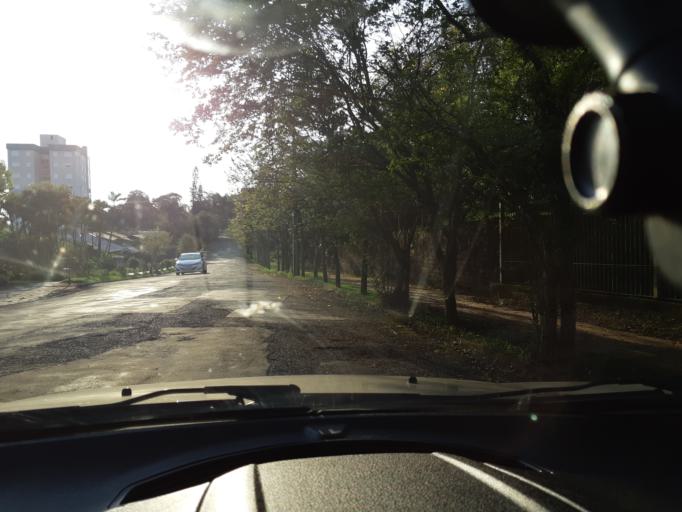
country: BR
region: Rio Grande do Sul
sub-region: Sao Leopoldo
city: Sao Leopoldo
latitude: -29.7777
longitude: -51.1368
